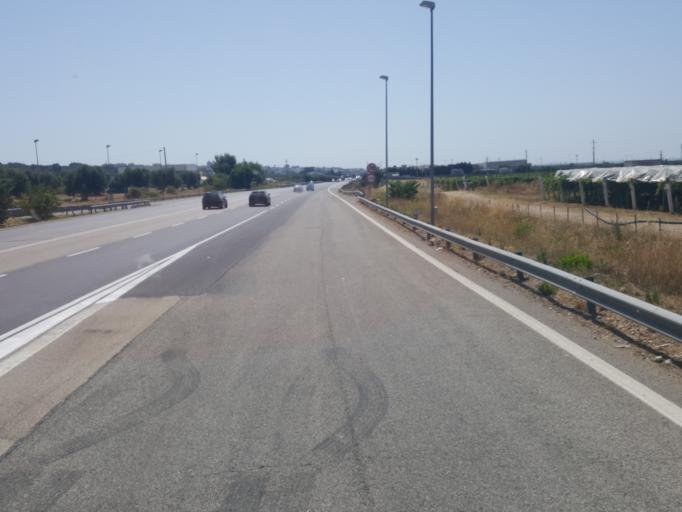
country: IT
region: Apulia
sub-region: Provincia di Taranto
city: Massafra
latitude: 40.5960
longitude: 17.0857
